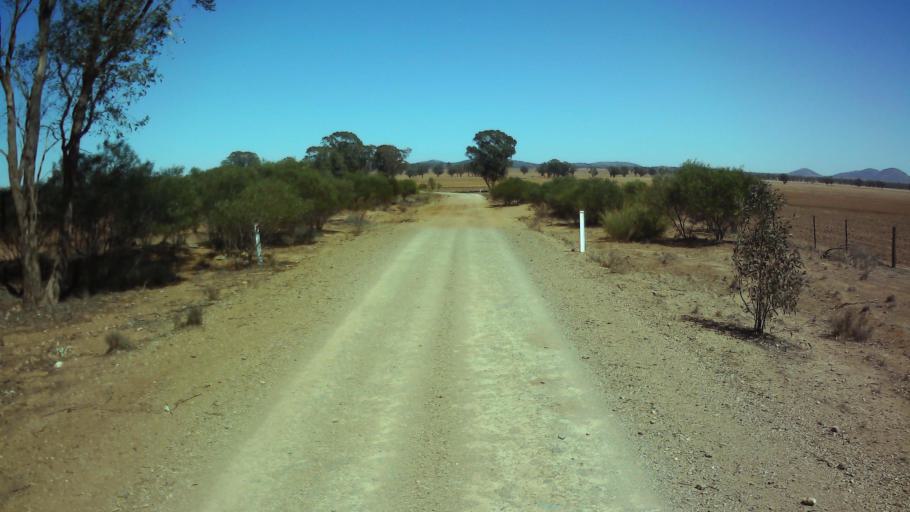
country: AU
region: New South Wales
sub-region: Forbes
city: Forbes
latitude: -33.6976
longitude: 147.8721
